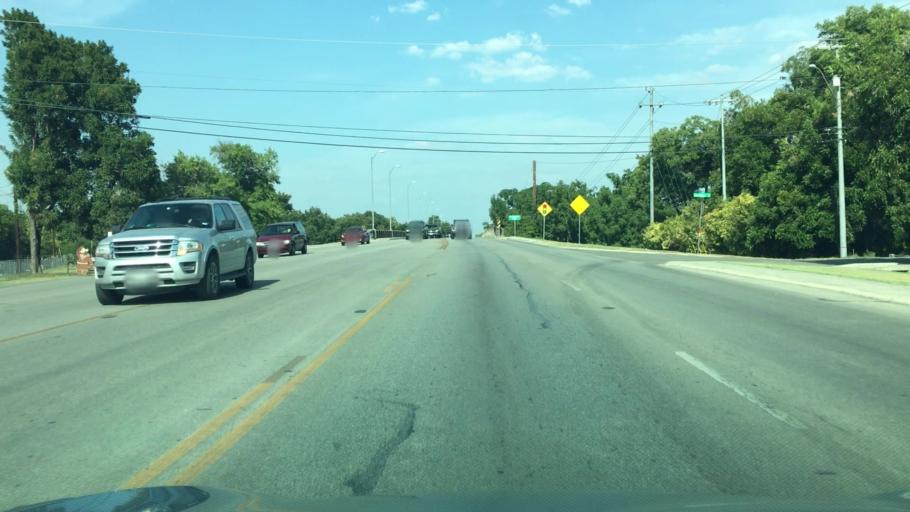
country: US
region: Texas
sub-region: Comal County
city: New Braunfels
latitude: 29.6940
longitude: -98.1094
